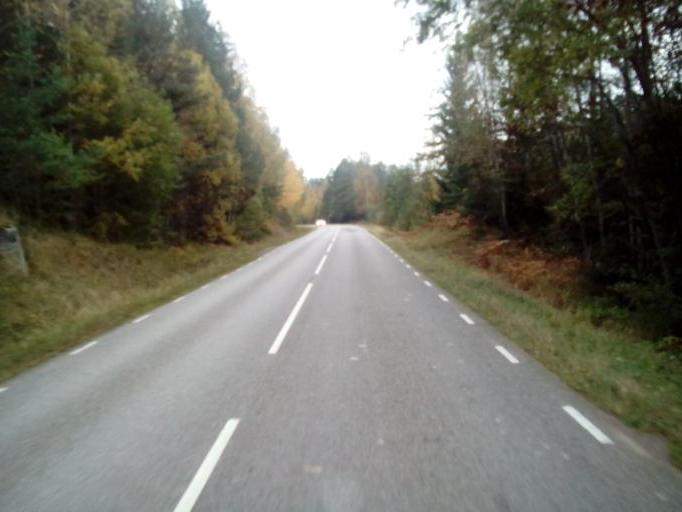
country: SE
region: Kalmar
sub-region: Vasterviks Kommun
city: Gamleby
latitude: 57.8712
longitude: 16.3063
